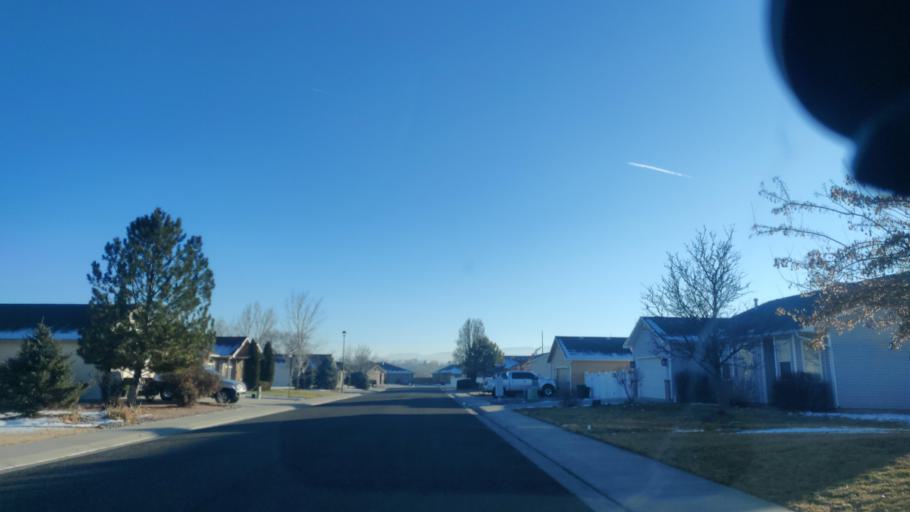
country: US
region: Colorado
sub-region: Mesa County
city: Grand Junction
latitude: 39.0610
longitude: -108.5213
